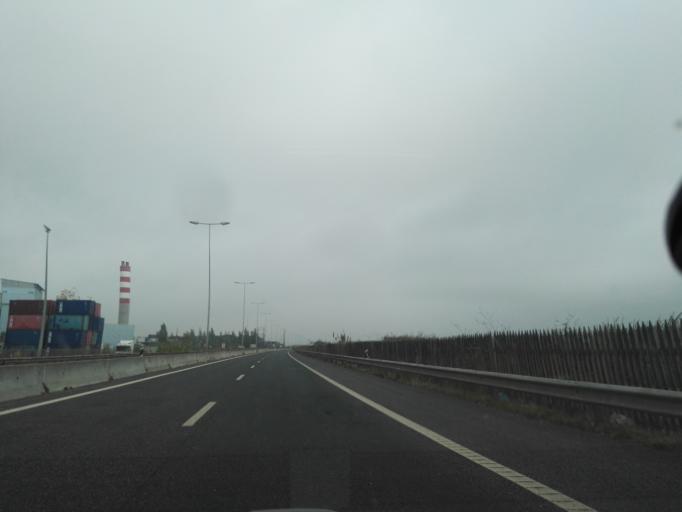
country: PT
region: Lisbon
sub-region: Loures
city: Sao Joao da Talha
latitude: 38.8241
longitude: -9.0838
